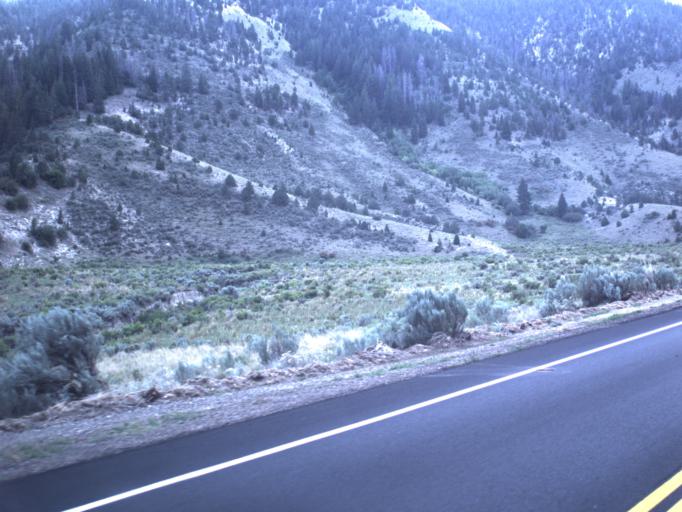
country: US
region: Utah
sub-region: Duchesne County
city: Duchesne
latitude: 39.9883
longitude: -110.6019
